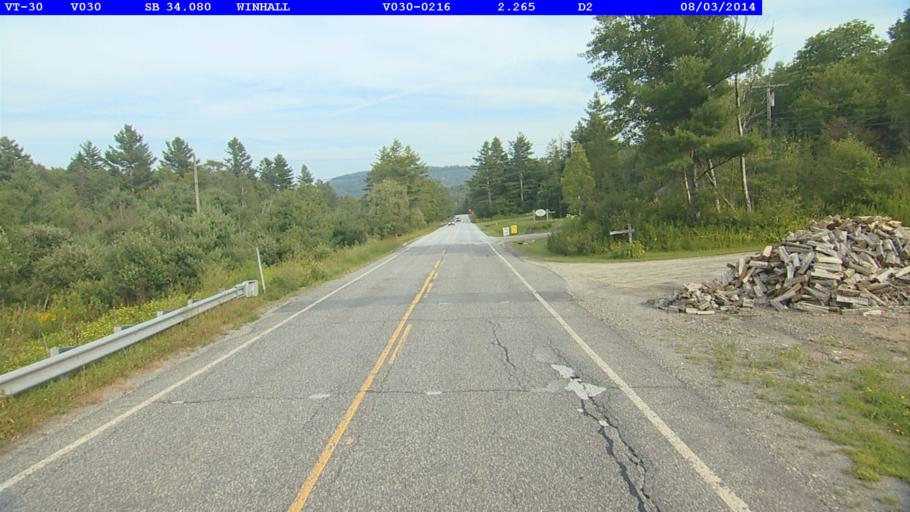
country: US
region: Vermont
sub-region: Bennington County
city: Manchester Center
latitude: 43.1515
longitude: -72.9077
